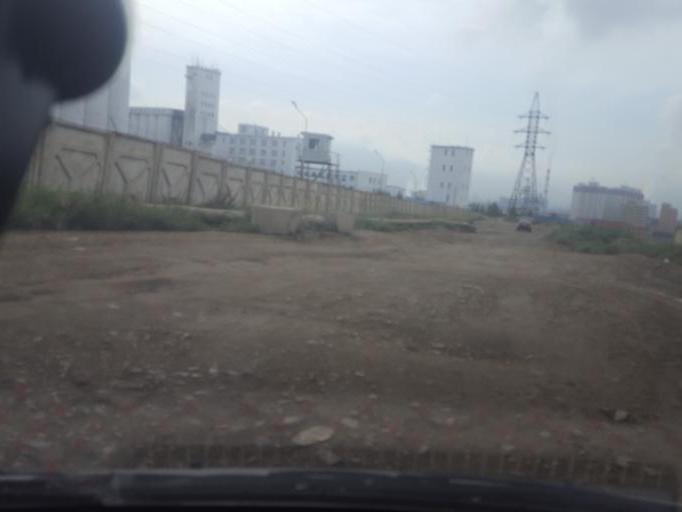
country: MN
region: Ulaanbaatar
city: Ulaanbaatar
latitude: 47.9179
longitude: 106.7998
